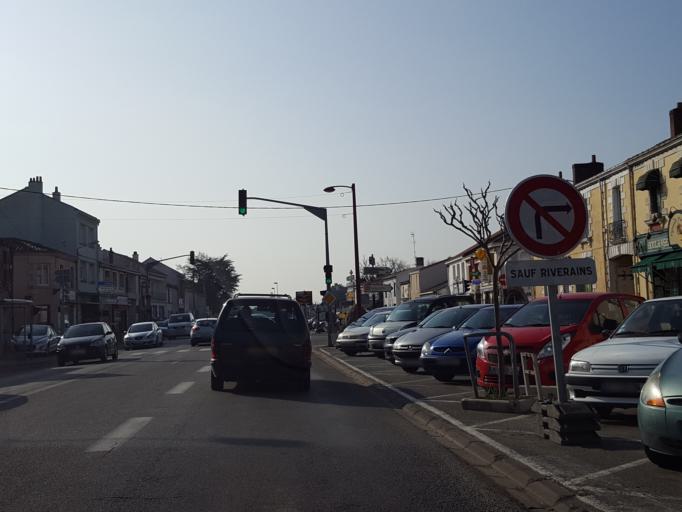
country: FR
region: Pays de la Loire
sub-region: Departement de la Loire-Atlantique
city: Geneston
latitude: 47.0561
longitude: -1.5128
